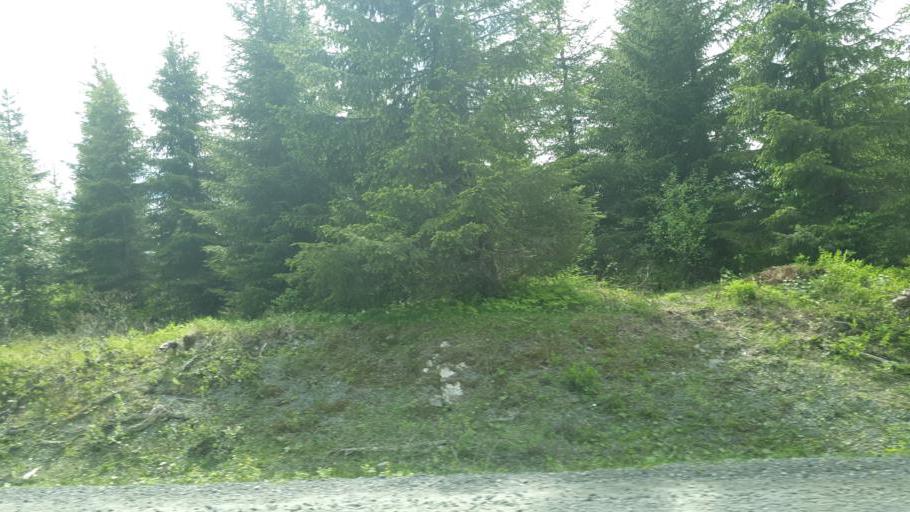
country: NO
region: Nord-Trondelag
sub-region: Leksvik
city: Leksvik
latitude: 63.6913
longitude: 10.4598
